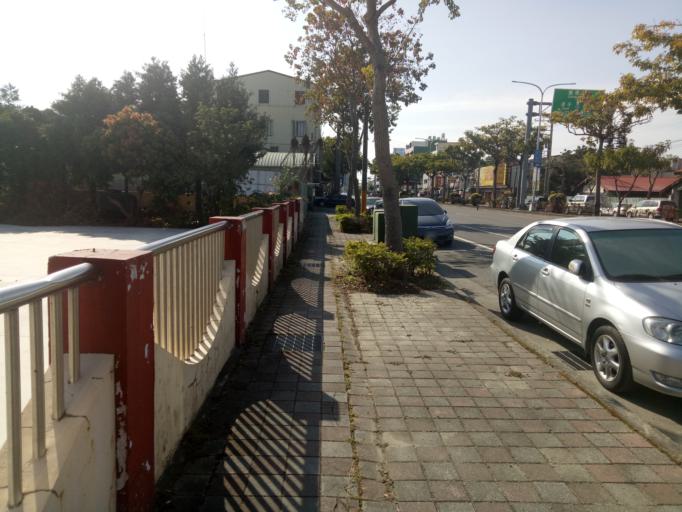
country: TW
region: Taiwan
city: Fengyuan
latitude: 24.2617
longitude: 120.7383
